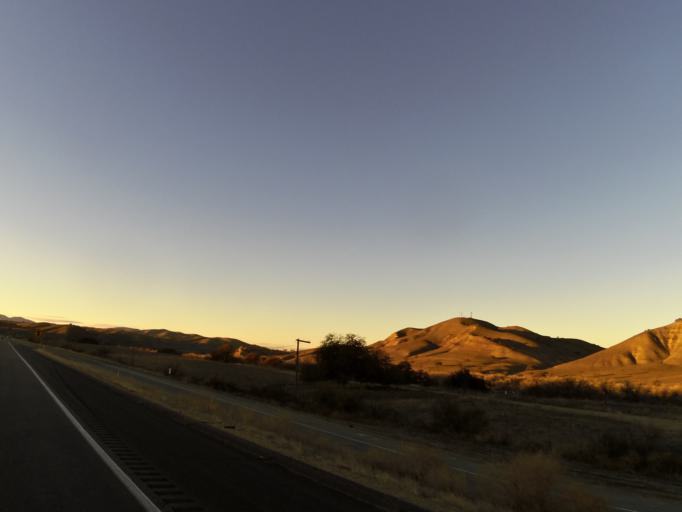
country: US
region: California
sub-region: San Luis Obispo County
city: Lake Nacimiento
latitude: 35.8652
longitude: -120.8186
